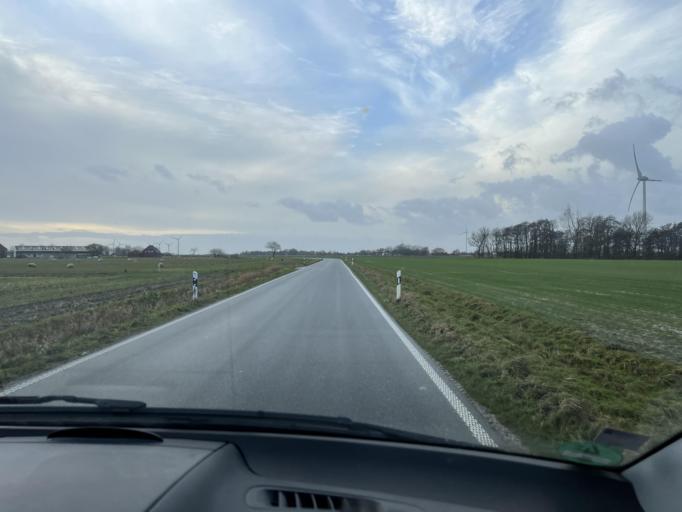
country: DE
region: Schleswig-Holstein
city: Suderdeich
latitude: 54.1950
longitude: 8.8999
